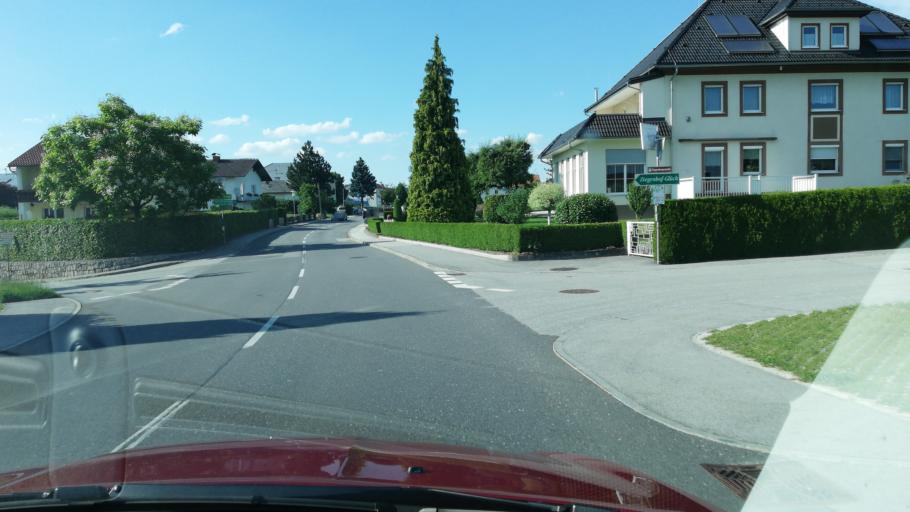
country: AT
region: Upper Austria
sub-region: Politischer Bezirk Steyr-Land
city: Waldneukirchen
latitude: 47.9928
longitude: 14.2174
